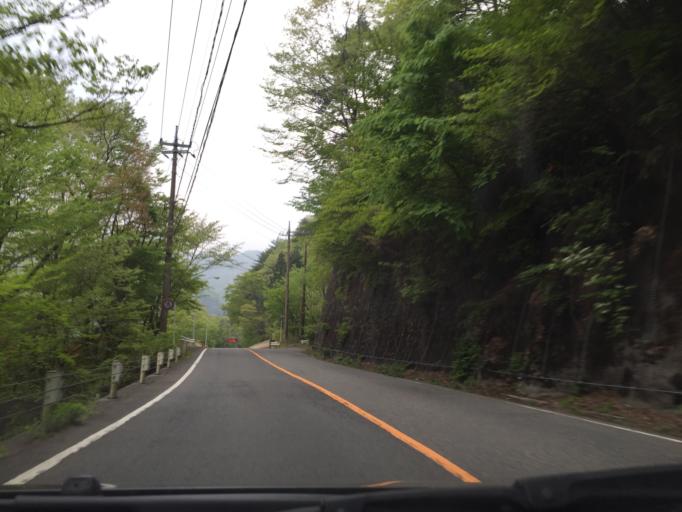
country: JP
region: Tochigi
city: Nikko
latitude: 36.8663
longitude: 139.7123
